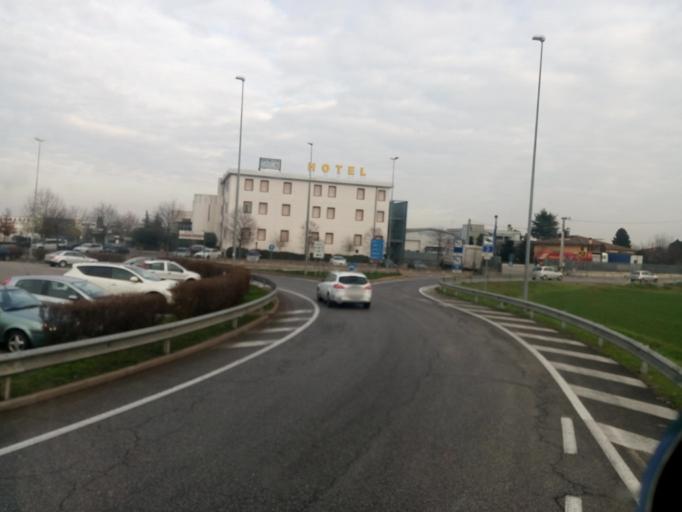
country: IT
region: Veneto
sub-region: Provincia di Verona
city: Pradelle
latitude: 45.2800
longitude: 10.8765
